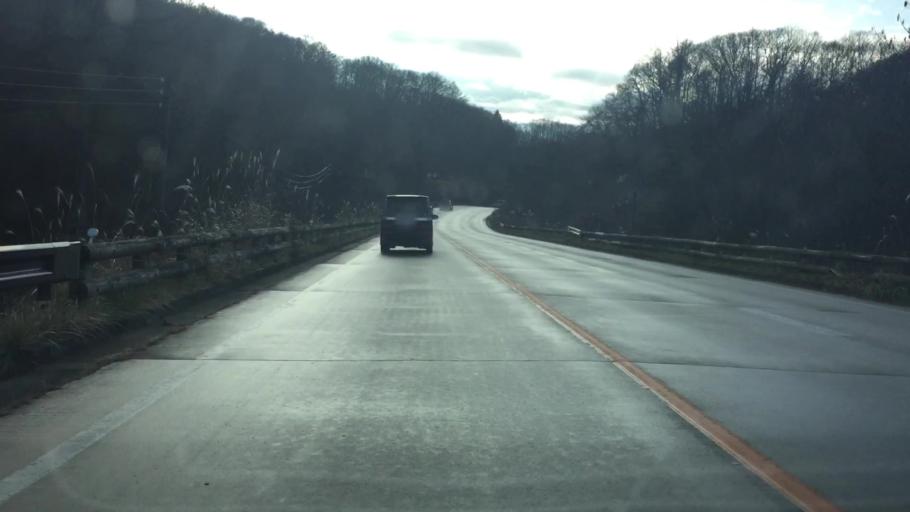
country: JP
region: Nagano
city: Saku
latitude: 36.3035
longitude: 138.6458
